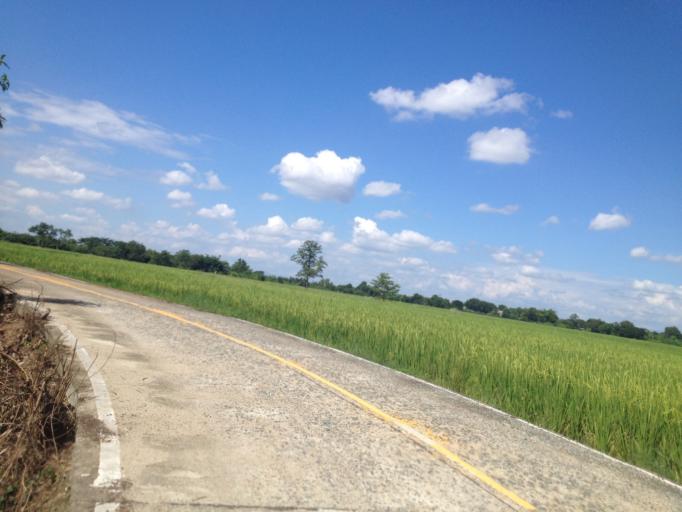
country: TH
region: Chiang Mai
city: Saraphi
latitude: 18.6902
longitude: 98.9804
